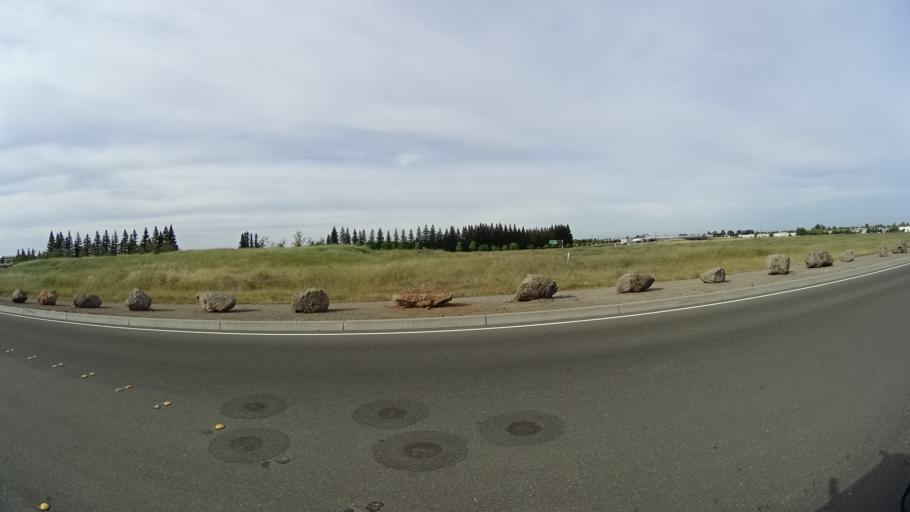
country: US
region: California
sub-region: Placer County
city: Rocklin
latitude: 38.8195
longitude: -121.2927
